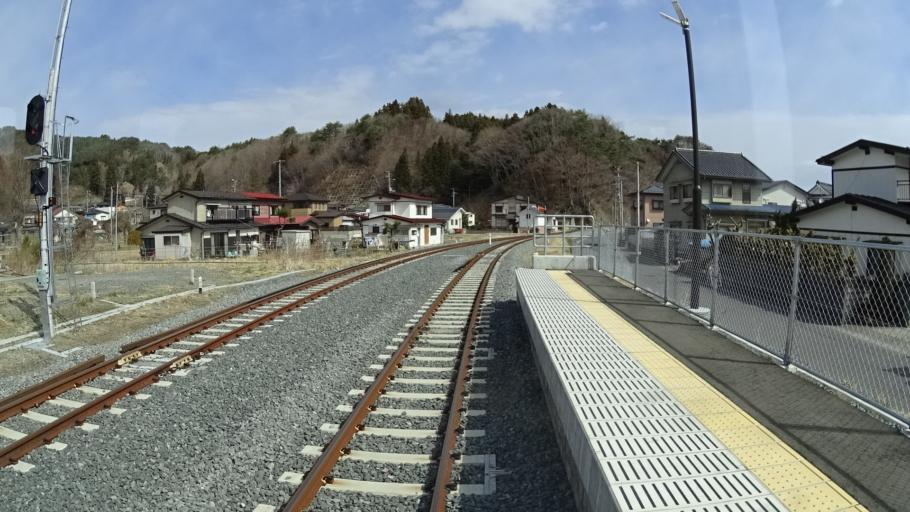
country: JP
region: Iwate
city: Miyako
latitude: 39.5817
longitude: 141.9379
